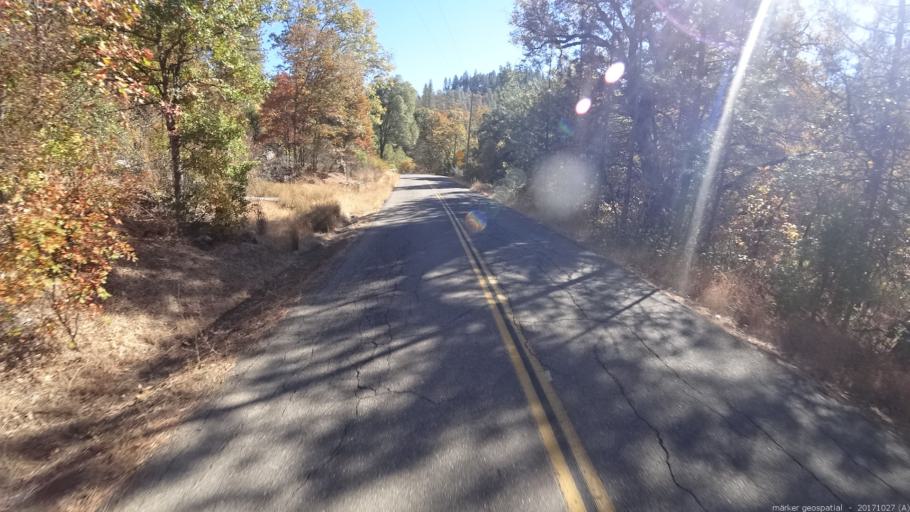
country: US
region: California
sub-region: Shasta County
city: Shingletown
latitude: 40.7494
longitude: -121.9455
